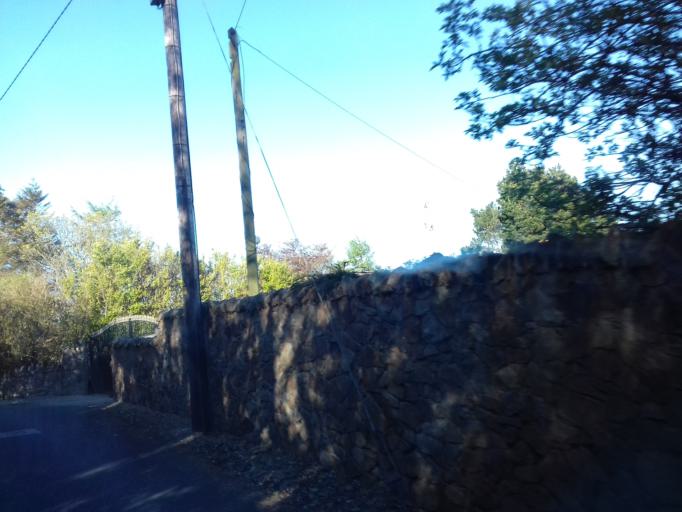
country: IE
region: Leinster
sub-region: Fingal County
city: Howth
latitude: 53.3695
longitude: -6.0632
